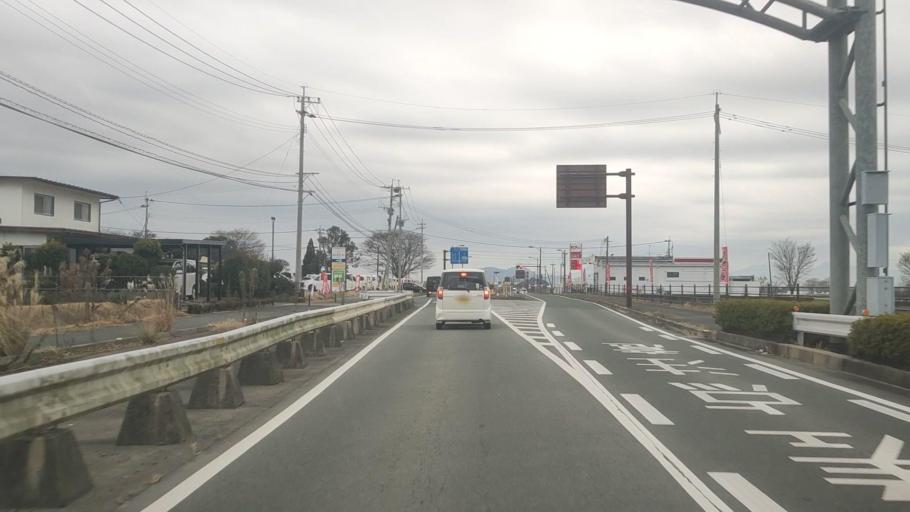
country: JP
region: Kumamoto
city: Ozu
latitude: 32.8477
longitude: 130.8365
